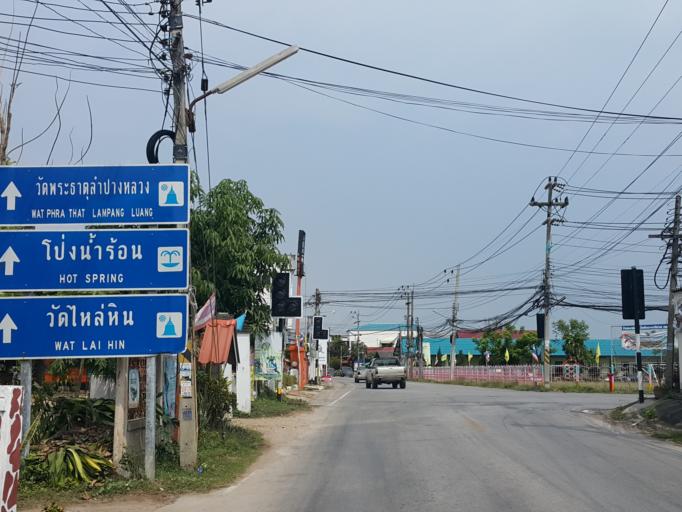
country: TH
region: Lampang
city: Ko Kha
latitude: 18.1908
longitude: 99.3945
